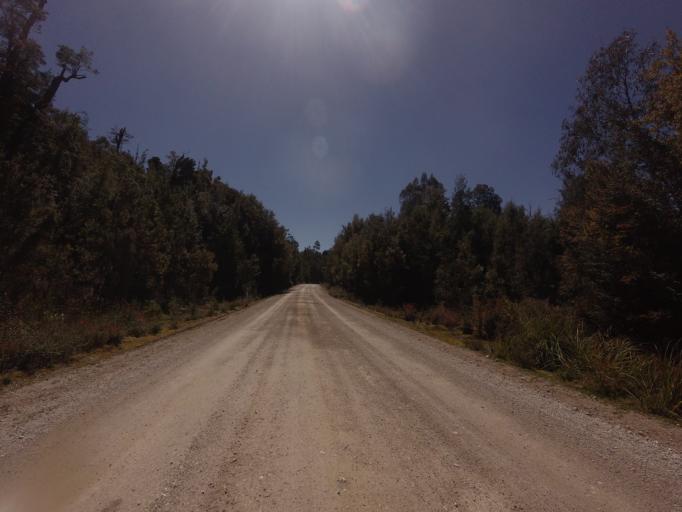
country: AU
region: Tasmania
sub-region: Huon Valley
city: Geeveston
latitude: -42.8301
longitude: 146.3860
